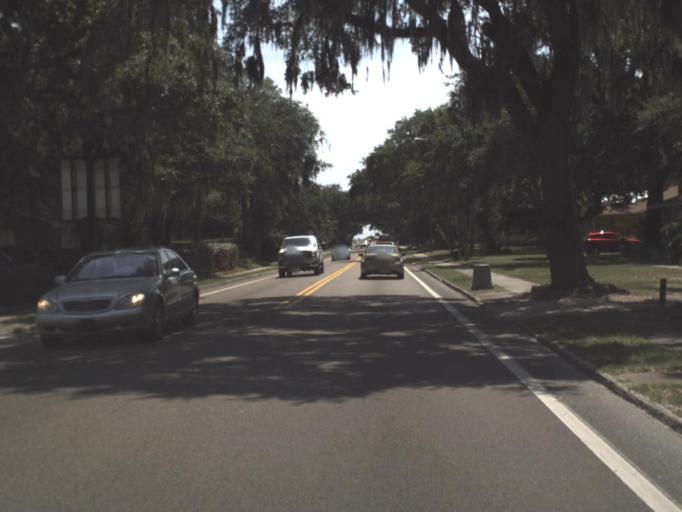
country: US
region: Florida
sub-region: Saint Johns County
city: Saint Augustine
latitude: 29.9097
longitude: -81.3190
